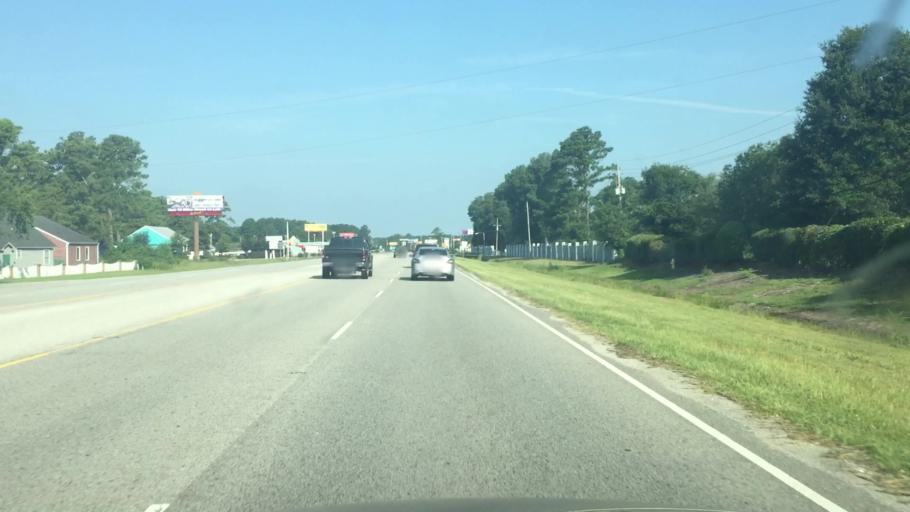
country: US
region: South Carolina
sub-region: Horry County
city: Little River
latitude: 33.8689
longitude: -78.6671
